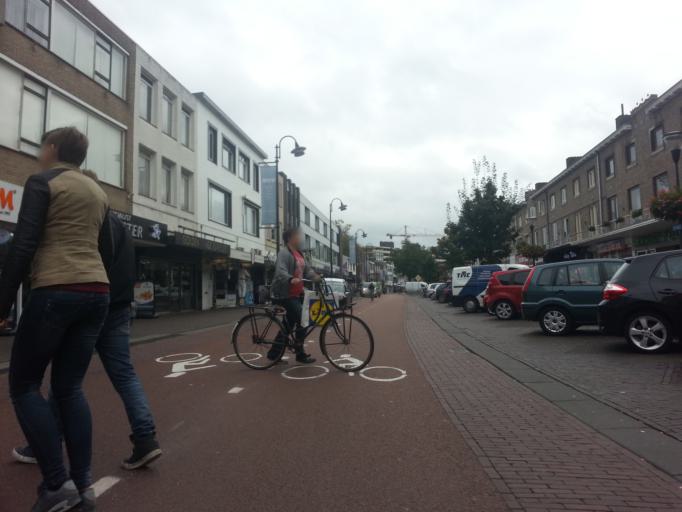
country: NL
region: North Brabant
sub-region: Gemeente Eindhoven
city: Eindhoven
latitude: 51.4496
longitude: 5.4739
